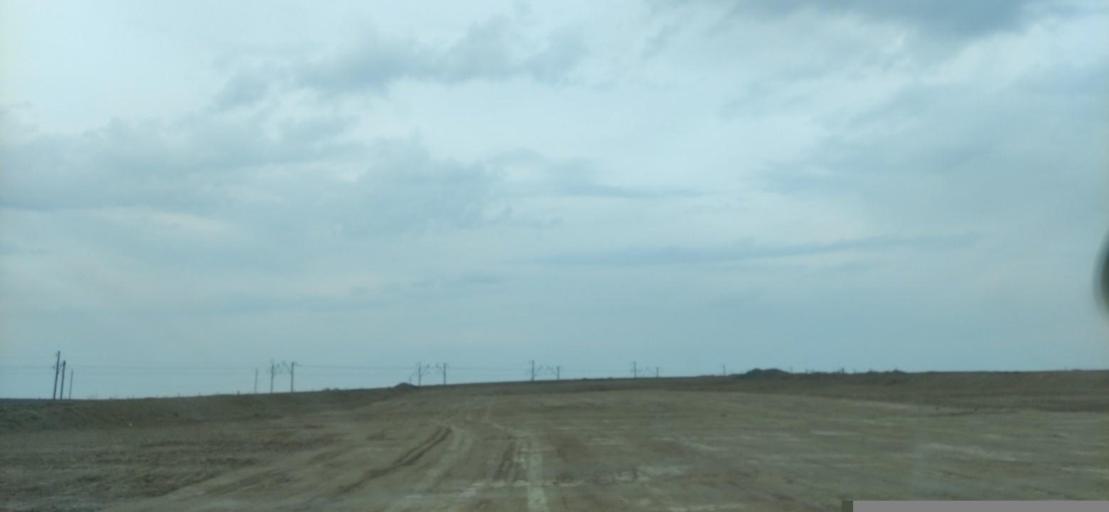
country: KZ
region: Qaraghandy
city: Saryshaghan
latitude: 46.0934
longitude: 73.6052
